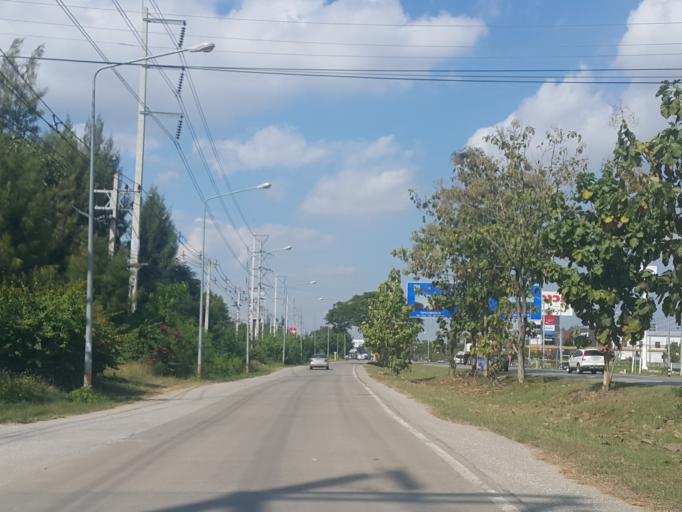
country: TH
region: Chiang Mai
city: Saraphi
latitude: 18.7408
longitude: 99.0356
